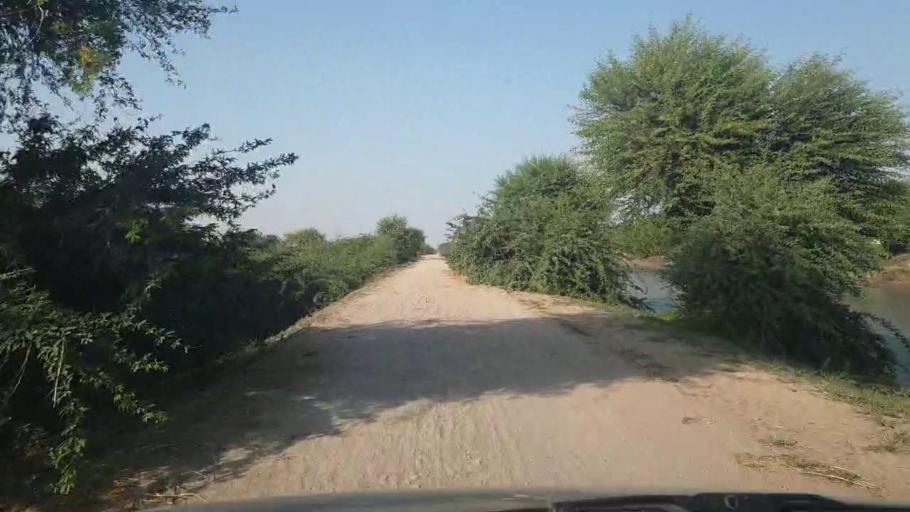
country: PK
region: Sindh
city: Badin
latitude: 24.6464
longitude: 68.8151
